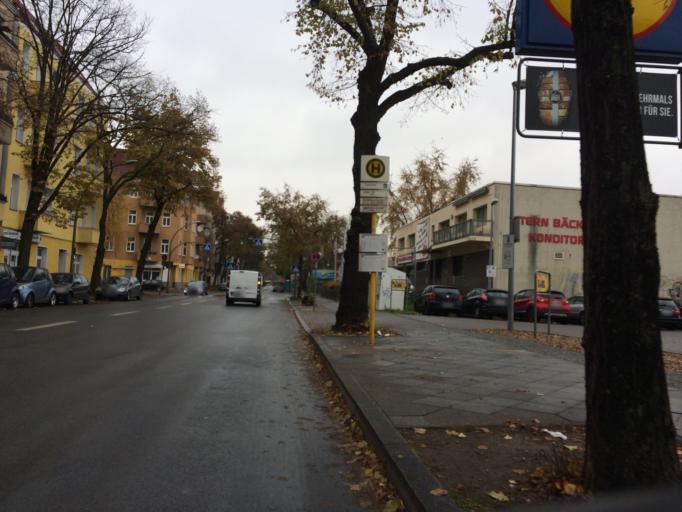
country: DE
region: Berlin
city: Gesundbrunnen
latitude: 52.5653
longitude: 13.3783
